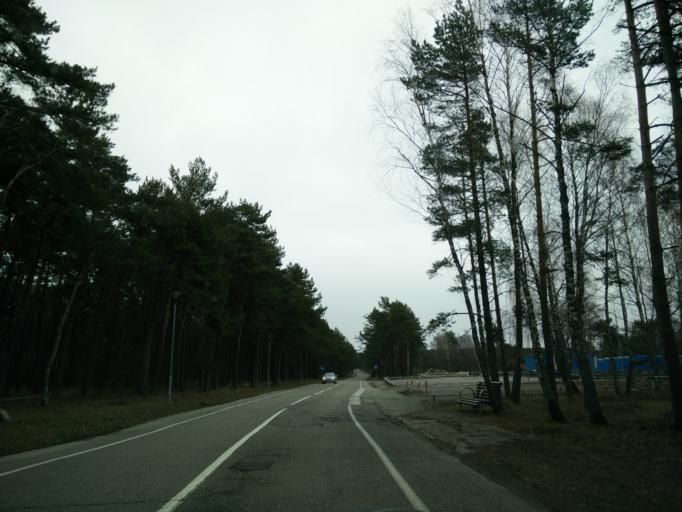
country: LT
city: Nida
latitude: 55.3010
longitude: 20.9859
